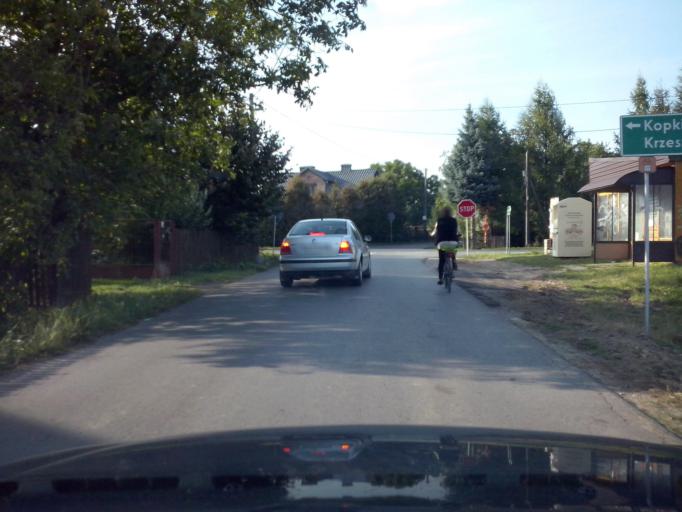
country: PL
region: Subcarpathian Voivodeship
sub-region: Powiat nizanski
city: Krzeszow
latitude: 50.3999
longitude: 22.3171
